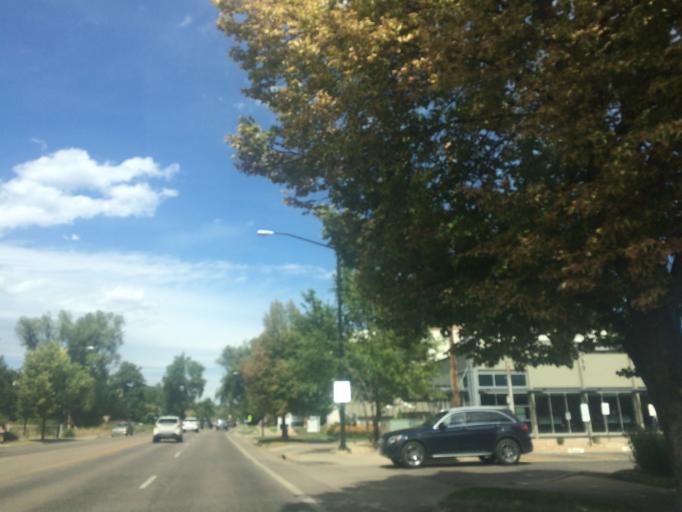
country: US
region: Colorado
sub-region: Boulder County
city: Boulder
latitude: 40.0180
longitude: -105.2630
